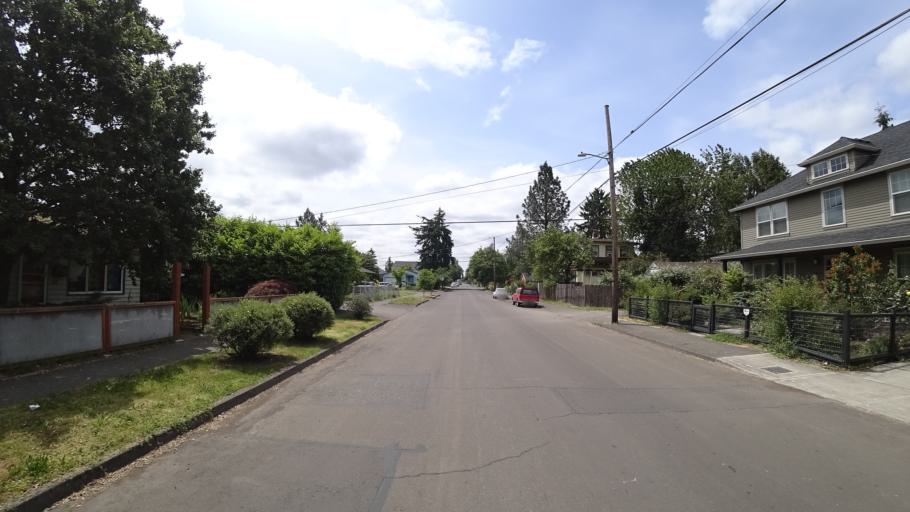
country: US
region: Oregon
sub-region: Multnomah County
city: Lents
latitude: 45.4807
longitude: -122.6022
